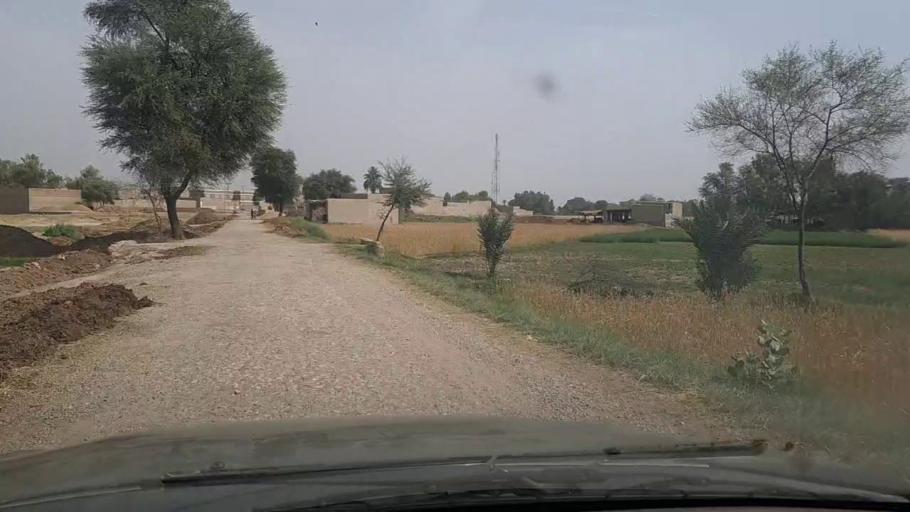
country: PK
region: Sindh
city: Chak
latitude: 27.8318
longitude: 68.7737
